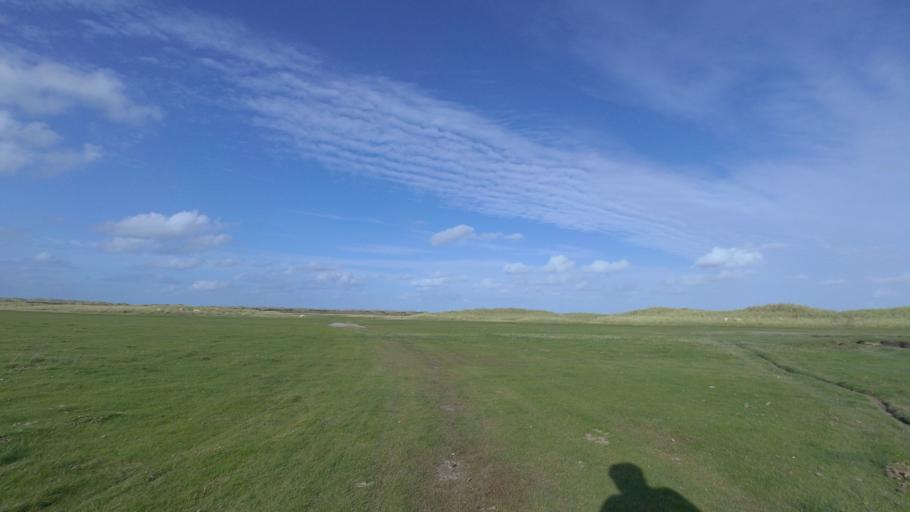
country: NL
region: Friesland
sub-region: Gemeente Ameland
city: Nes
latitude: 53.4543
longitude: 5.8634
